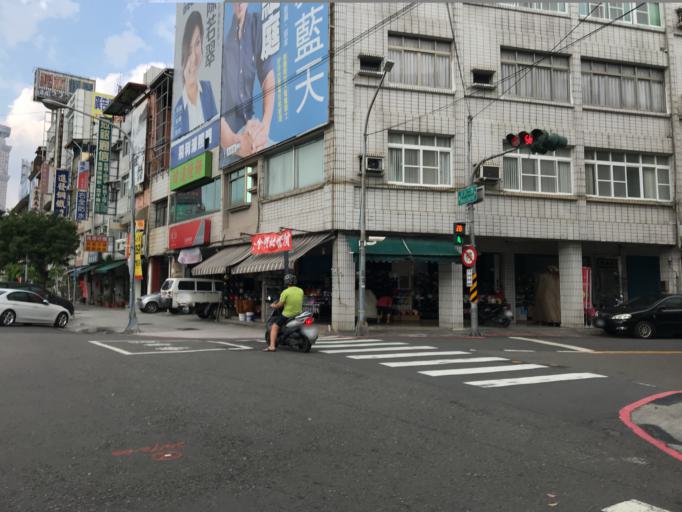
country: TW
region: Kaohsiung
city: Kaohsiung
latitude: 22.6351
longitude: 120.3138
